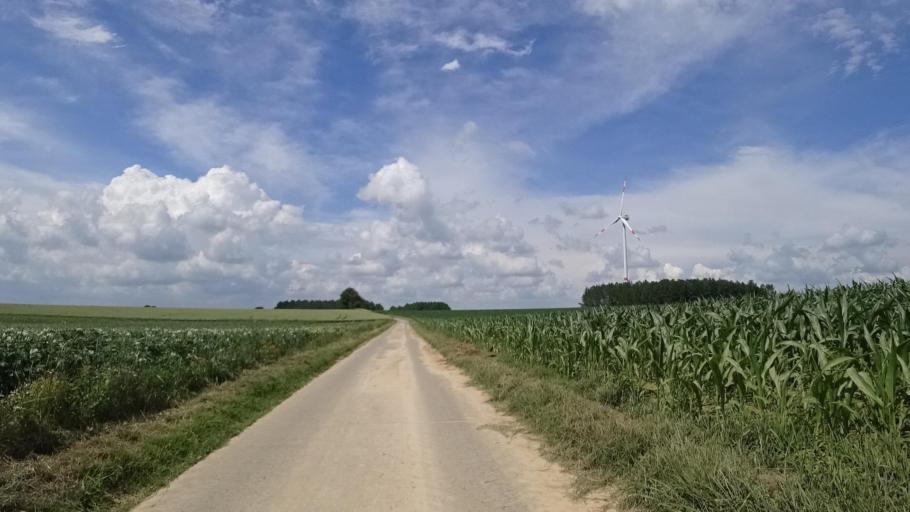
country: BE
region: Wallonia
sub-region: Province du Brabant Wallon
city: Perwez
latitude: 50.6025
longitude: 4.7755
